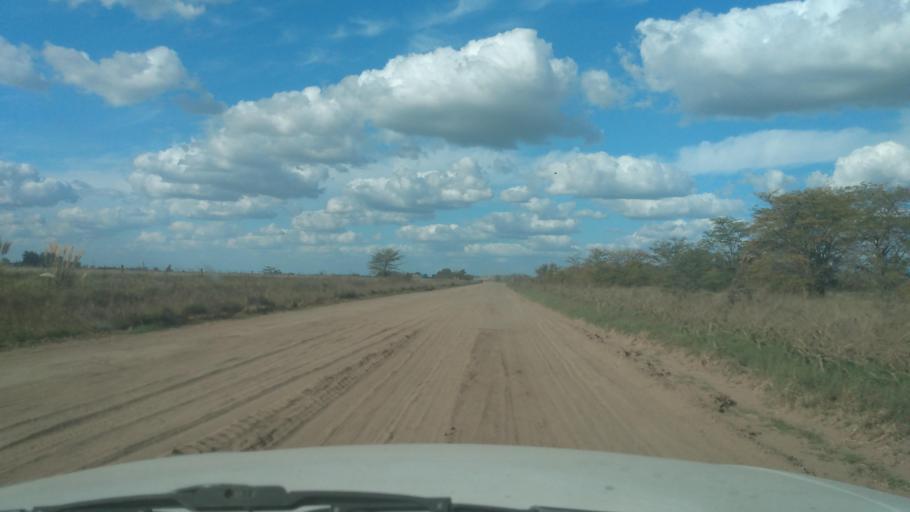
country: AR
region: Buenos Aires
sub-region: Partido de Navarro
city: Navarro
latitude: -35.0115
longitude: -59.4286
